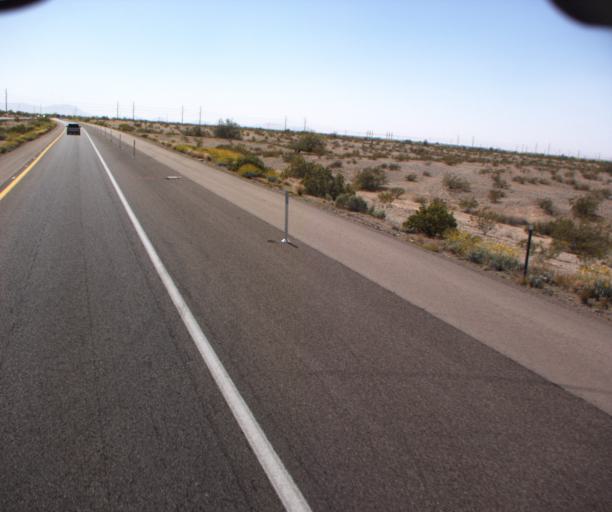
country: US
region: Arizona
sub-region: Maricopa County
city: Gila Bend
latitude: 32.9804
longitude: -112.6687
